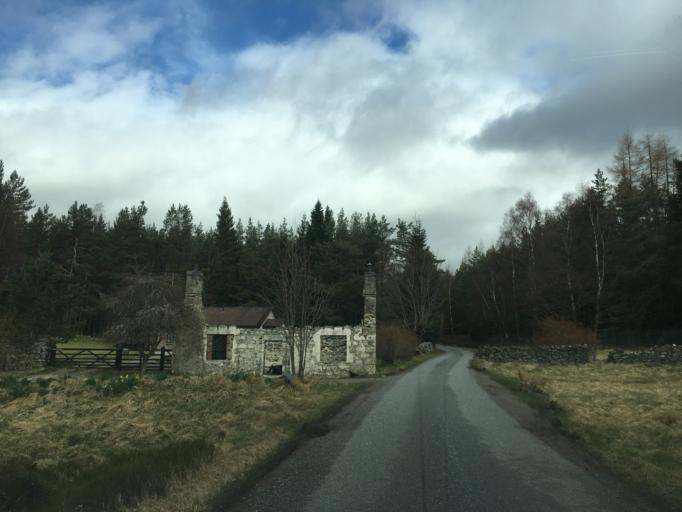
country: GB
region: Scotland
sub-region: Highland
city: Kingussie
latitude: 57.1007
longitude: -3.9213
